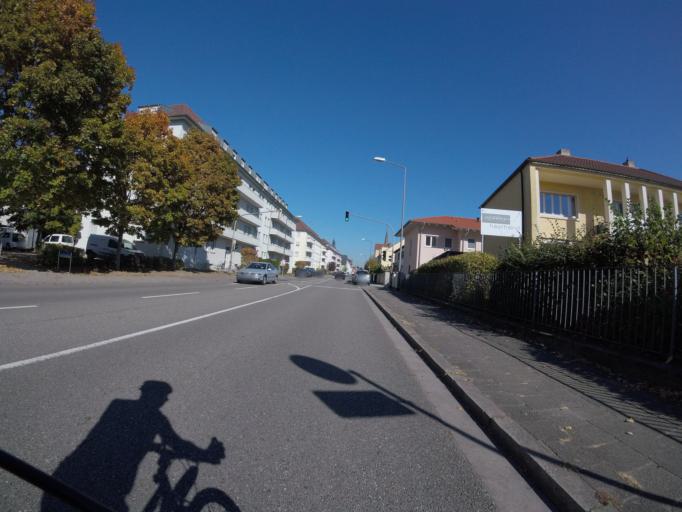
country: DE
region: Rheinland-Pfalz
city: Speyer
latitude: 49.3108
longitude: 8.4262
